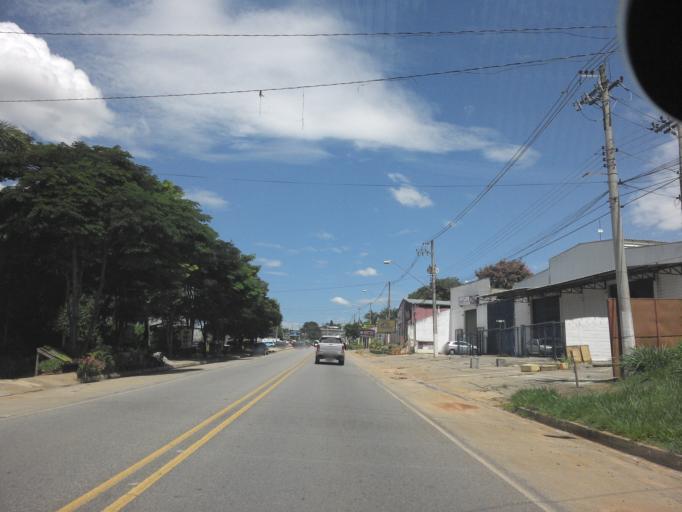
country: BR
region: Sao Paulo
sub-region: Taubate
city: Taubate
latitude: -23.0541
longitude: -45.5553
